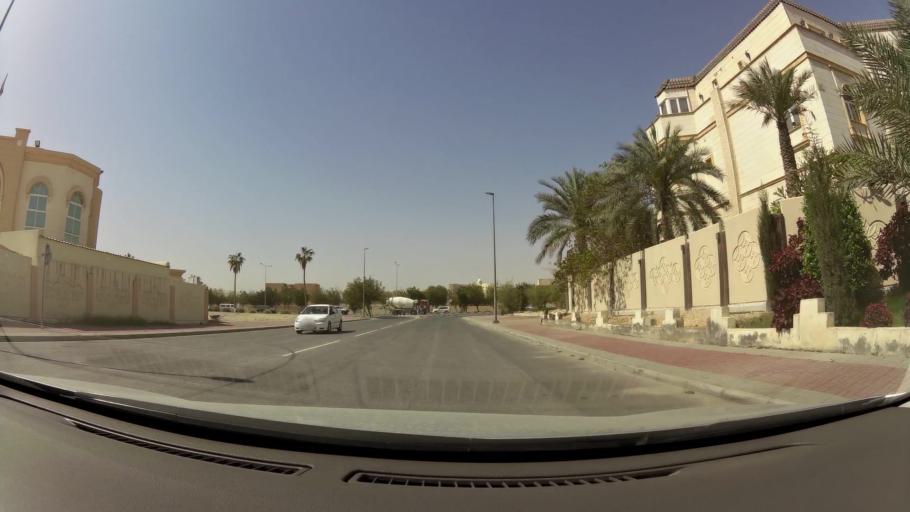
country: QA
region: Baladiyat ad Dawhah
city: Doha
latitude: 25.3549
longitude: 51.4977
